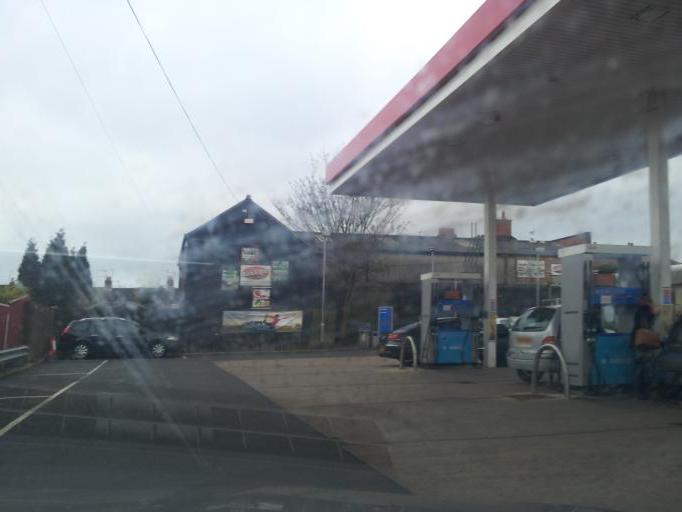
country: GB
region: England
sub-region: Northamptonshire
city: Kettering
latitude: 52.4004
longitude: -0.7119
